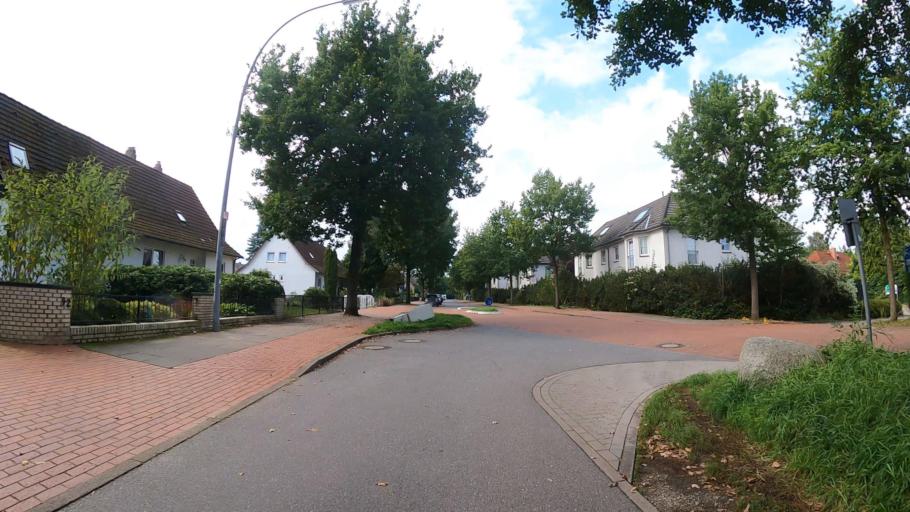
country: DE
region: Schleswig-Holstein
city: Kolln-Reisiek
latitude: 53.7329
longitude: 9.6777
